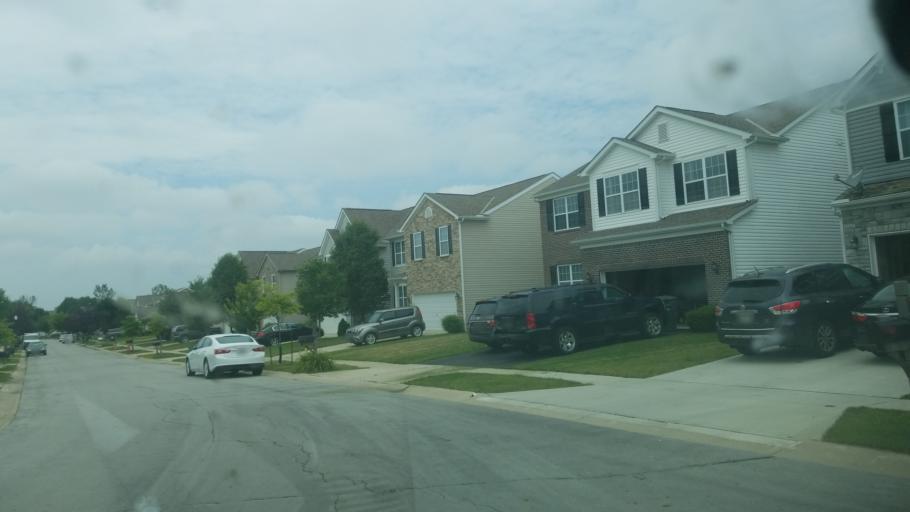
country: US
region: Ohio
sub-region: Franklin County
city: Reynoldsburg
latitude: 40.0021
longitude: -82.7818
